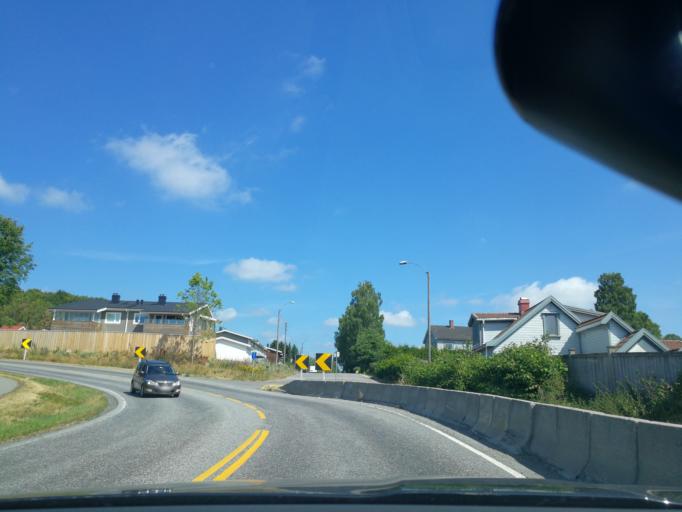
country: NO
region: Vestfold
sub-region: Sandefjord
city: Sandefjord
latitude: 59.1731
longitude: 10.2120
